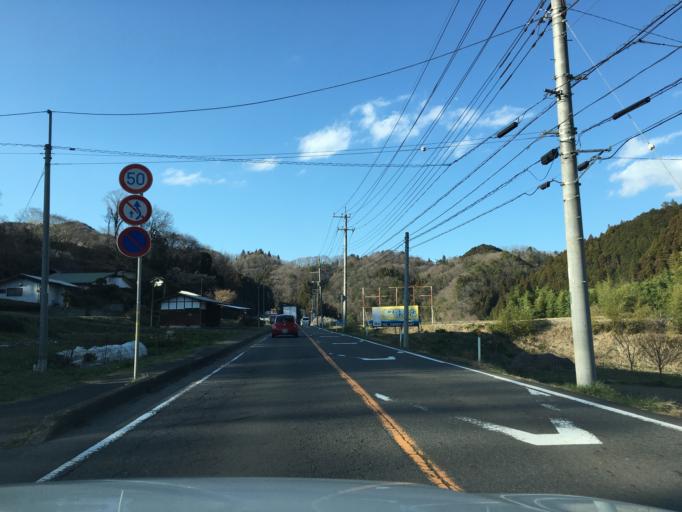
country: JP
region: Ibaraki
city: Daigo
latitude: 36.7320
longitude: 140.3903
